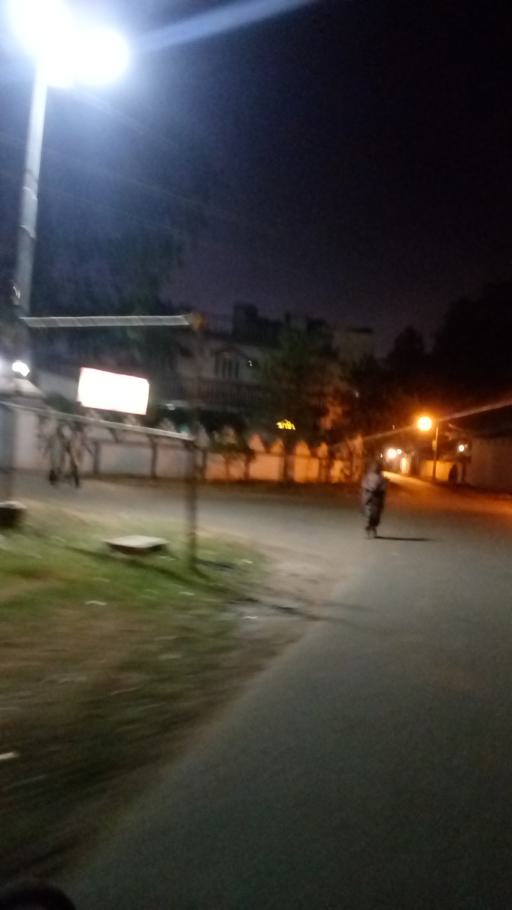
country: IN
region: Odisha
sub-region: Cuttack
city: Cuttack
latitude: 20.4849
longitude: 85.8665
